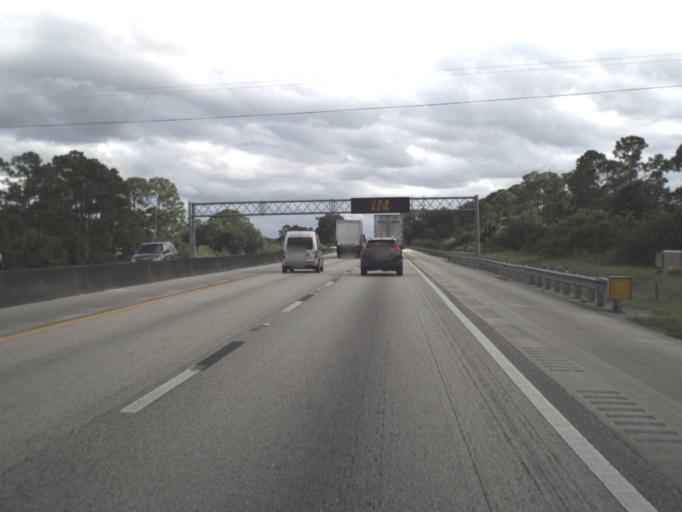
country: US
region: Florida
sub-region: Palm Beach County
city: Limestone Creek
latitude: 26.9750
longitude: -80.1807
